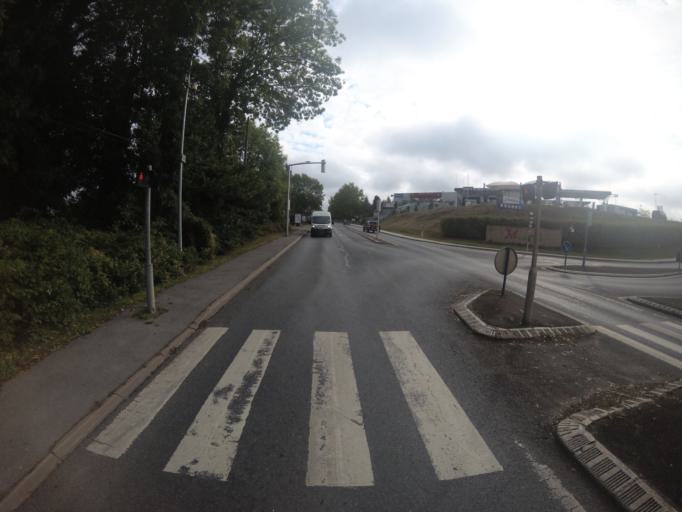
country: FR
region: Ile-de-France
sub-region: Departement de Seine-et-Marne
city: Montevrain
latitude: 48.8781
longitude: 2.7490
